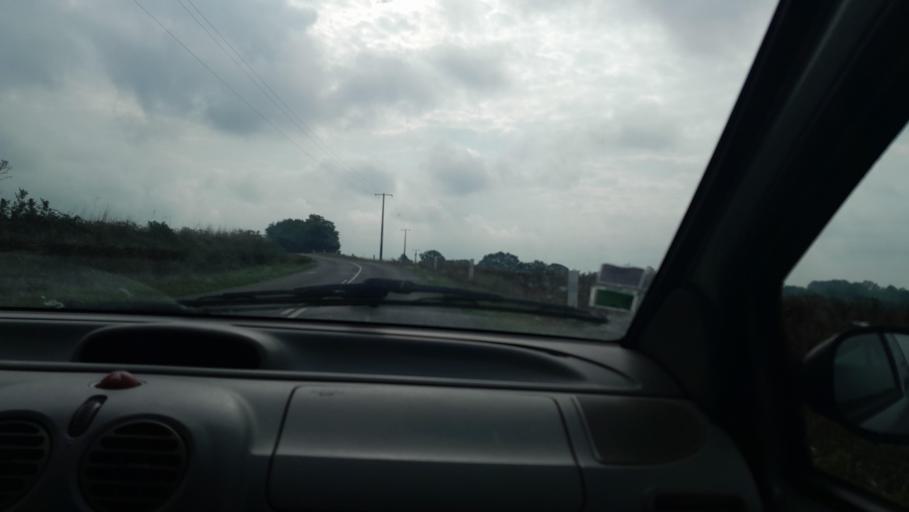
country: FR
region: Pays de la Loire
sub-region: Departement de la Mayenne
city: Cosse-le-Vivien
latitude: 47.9563
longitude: -0.9665
